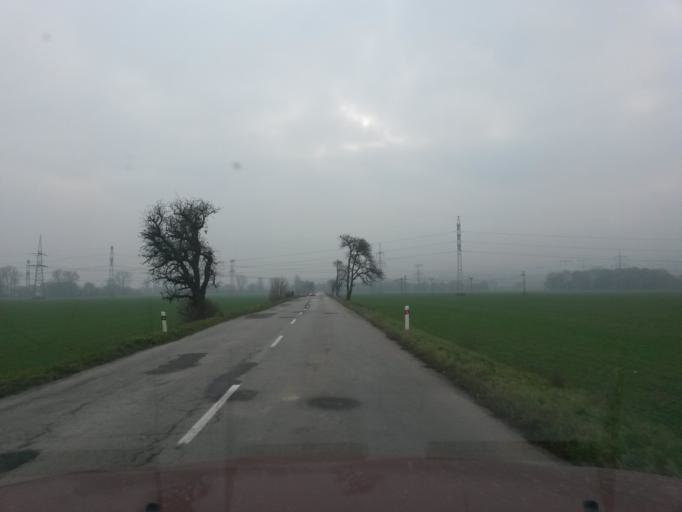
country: SK
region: Presovsky
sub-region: Okres Presov
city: Presov
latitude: 48.8671
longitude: 21.2712
